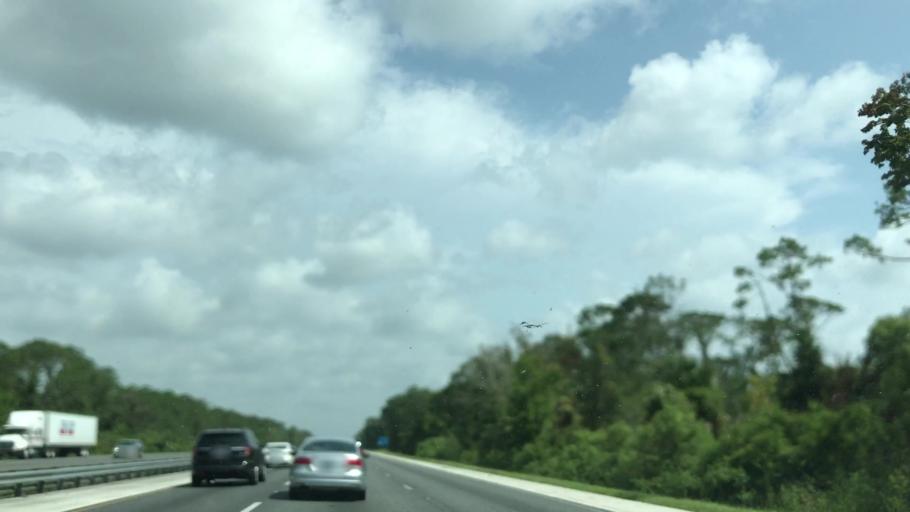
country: US
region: Florida
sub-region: Volusia County
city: Ormond-by-the-Sea
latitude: 29.3853
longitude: -81.1470
